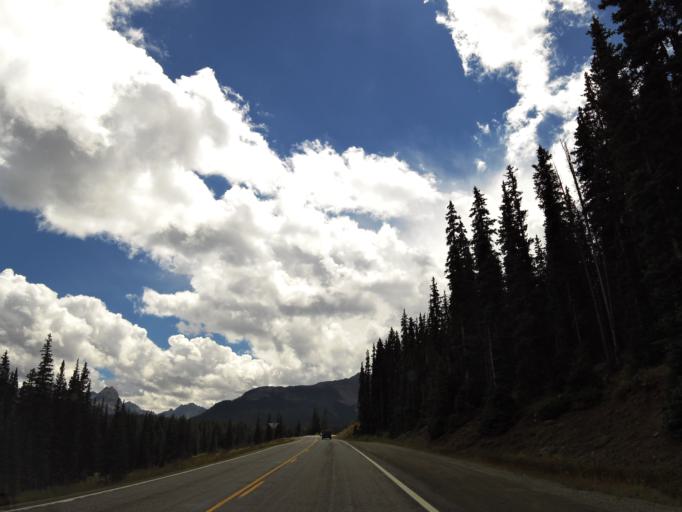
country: US
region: Colorado
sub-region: San Juan County
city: Silverton
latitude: 37.7603
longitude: -107.6807
